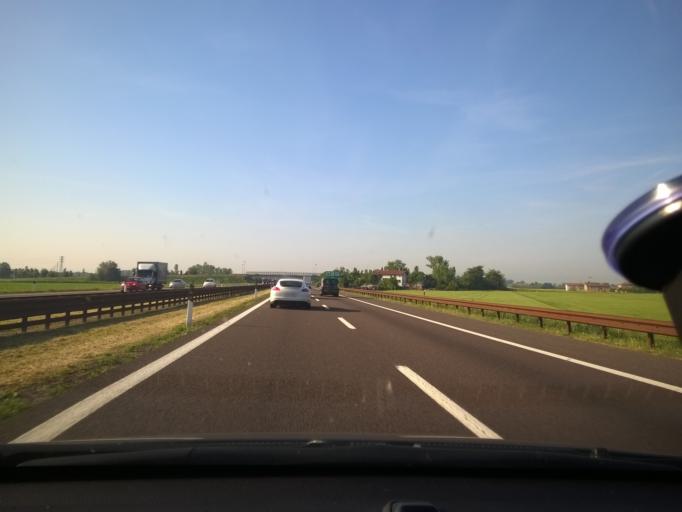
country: IT
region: Emilia-Romagna
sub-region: Provincia di Modena
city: Campogalliano
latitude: 44.7103
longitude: 10.8475
